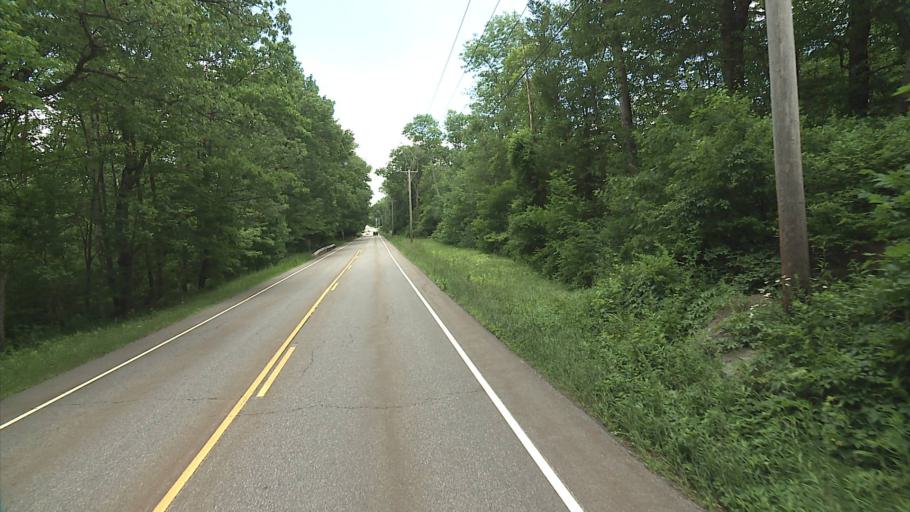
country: US
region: Connecticut
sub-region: Litchfield County
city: West Torrington
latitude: 41.8536
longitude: -73.2437
